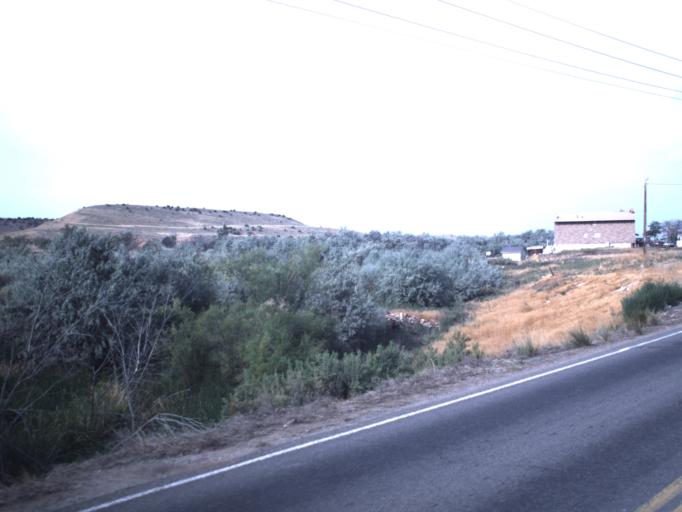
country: US
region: Utah
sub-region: Duchesne County
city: Roosevelt
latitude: 40.2586
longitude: -110.0650
